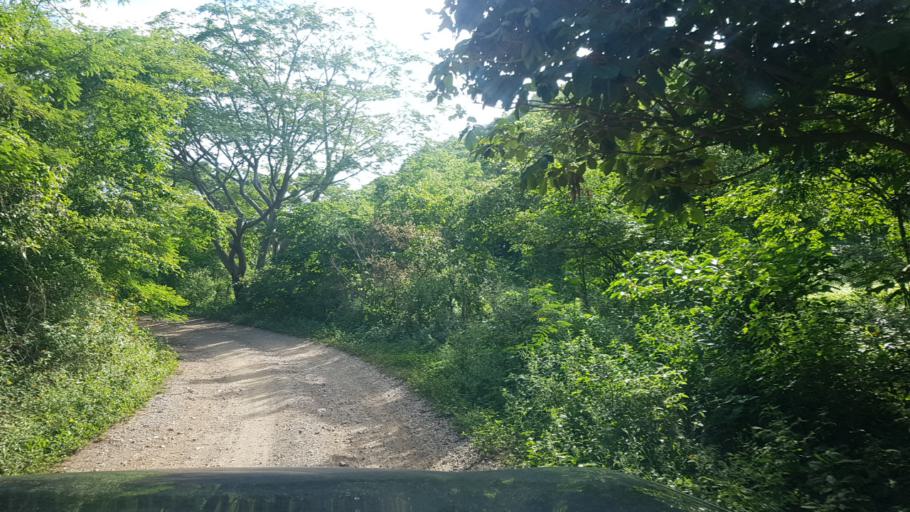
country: NI
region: Nueva Segovia
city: Ocotal
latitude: 13.6065
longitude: -86.4653
